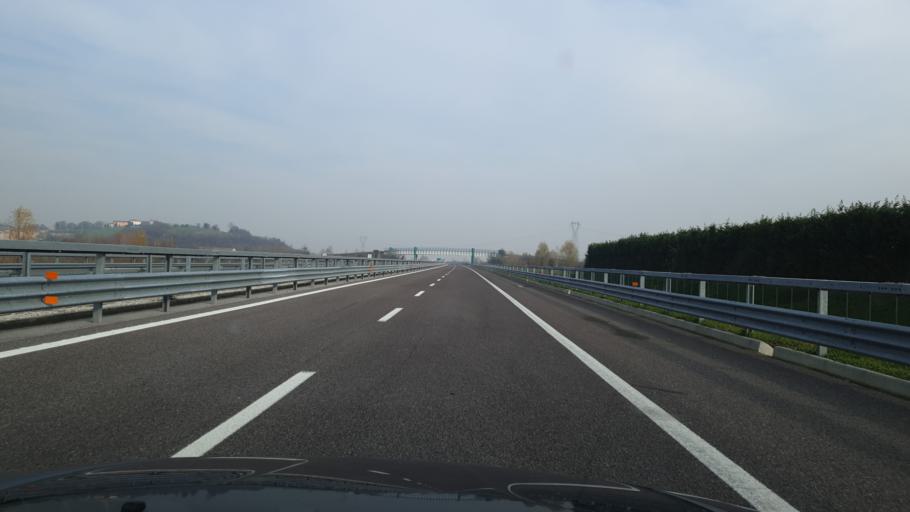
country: IT
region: Veneto
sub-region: Provincia di Vicenza
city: Albettone
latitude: 45.3547
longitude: 11.5984
